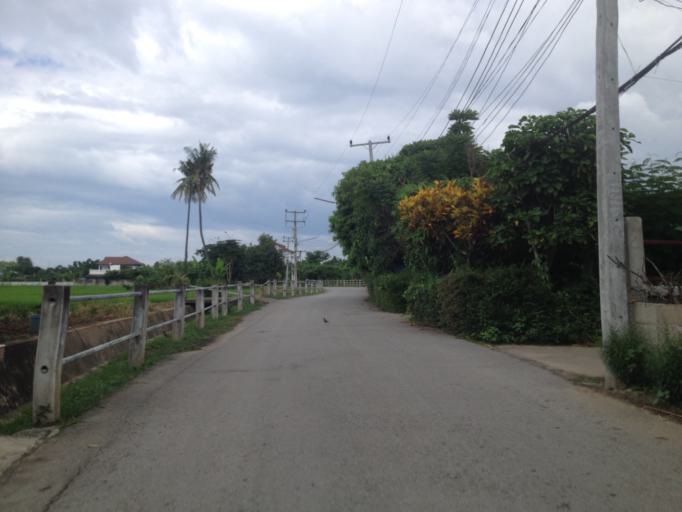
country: TH
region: Chiang Mai
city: Hang Dong
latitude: 18.6962
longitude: 98.9110
